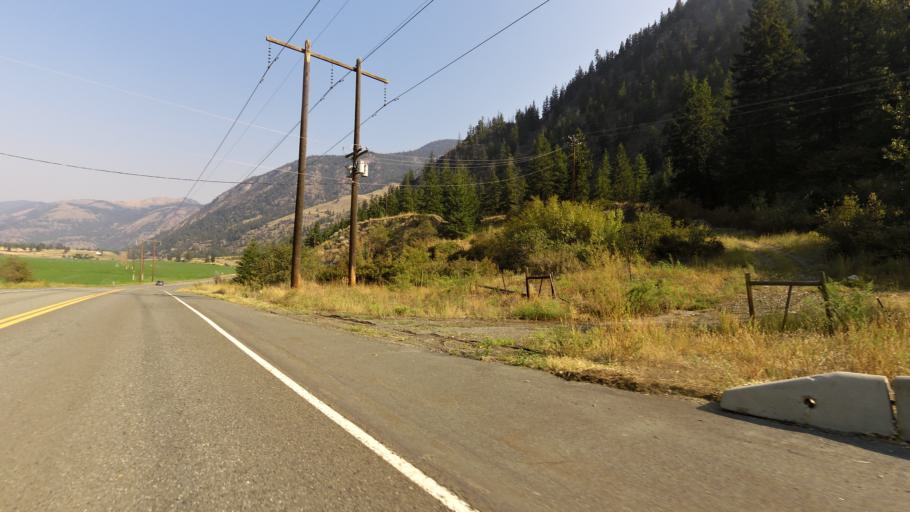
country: CA
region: British Columbia
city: Summerland
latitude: 49.3269
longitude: -120.0460
